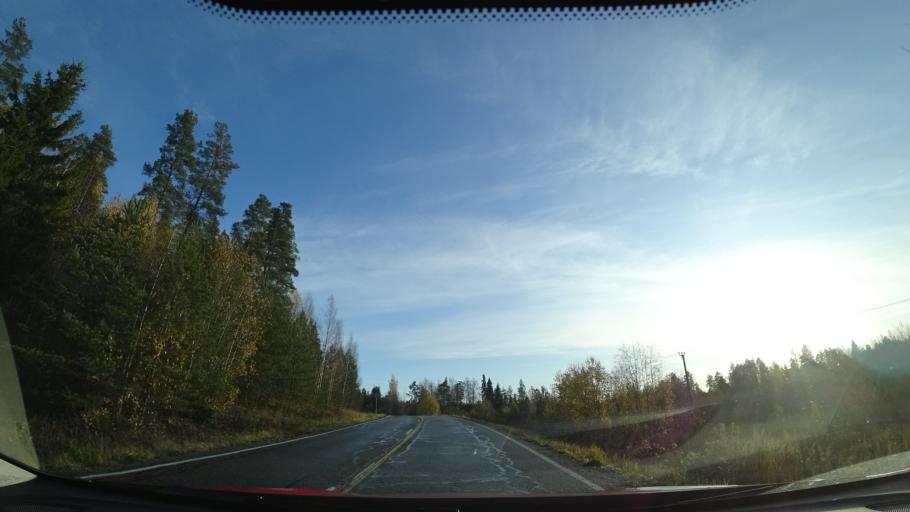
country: FI
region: Uusimaa
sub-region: Helsinki
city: Sibbo
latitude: 60.2729
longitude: 25.2016
